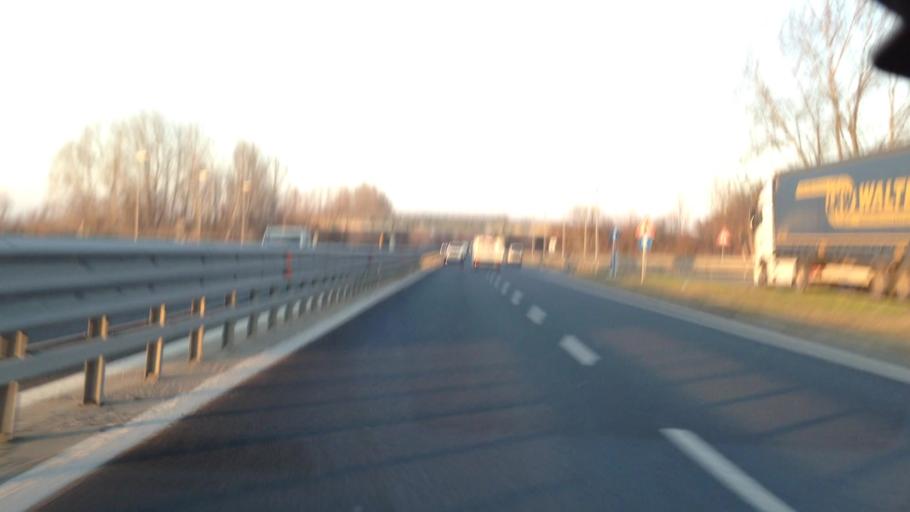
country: IT
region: Piedmont
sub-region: Provincia di Asti
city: Mongardino
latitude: 44.8650
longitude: 8.2056
